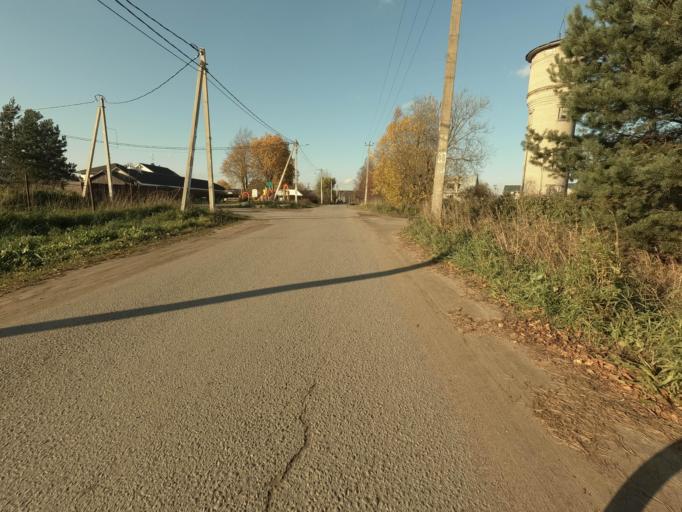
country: RU
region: Leningrad
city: Luppolovo
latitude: 60.1352
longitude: 30.2570
